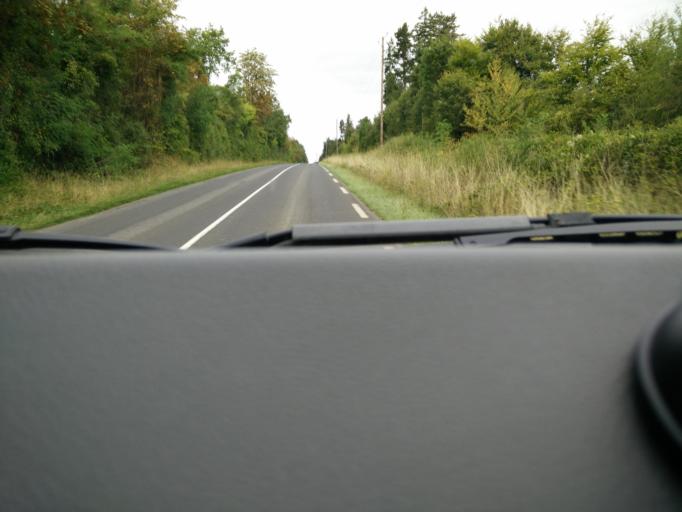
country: FR
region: Lorraine
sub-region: Departement de Meurthe-et-Moselle
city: Montauville
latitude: 48.9127
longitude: 5.9248
